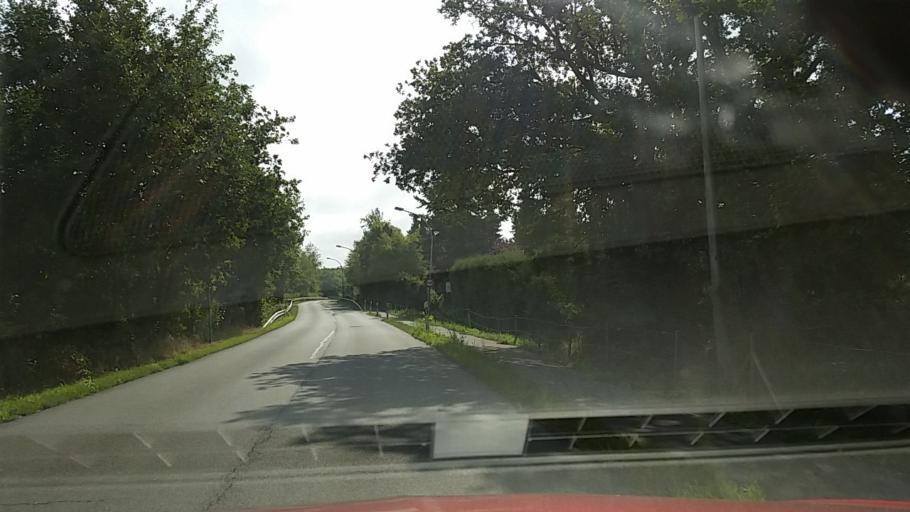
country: DE
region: Schleswig-Holstein
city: Pinneberg
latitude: 53.6305
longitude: 9.7740
